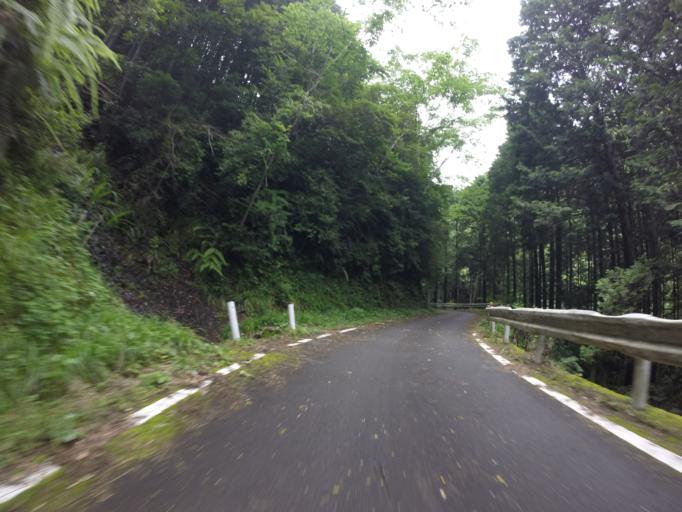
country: JP
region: Shizuoka
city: Shizuoka-shi
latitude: 35.0286
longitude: 138.3030
